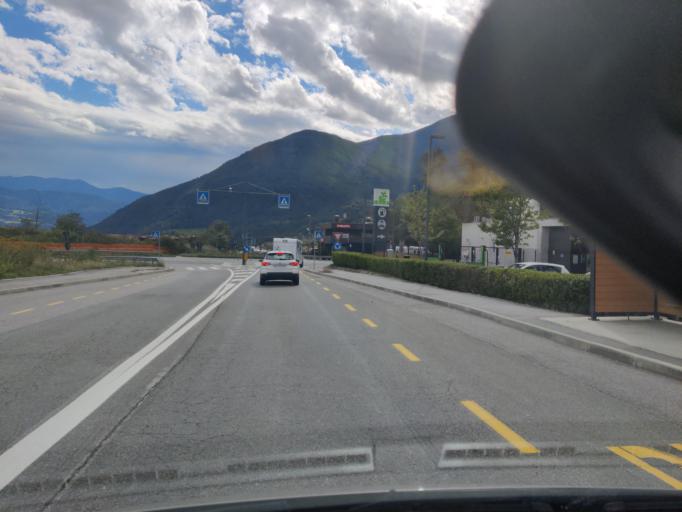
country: IT
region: Trentino-Alto Adige
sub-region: Bolzano
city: Varna
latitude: 46.7591
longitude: 11.6383
